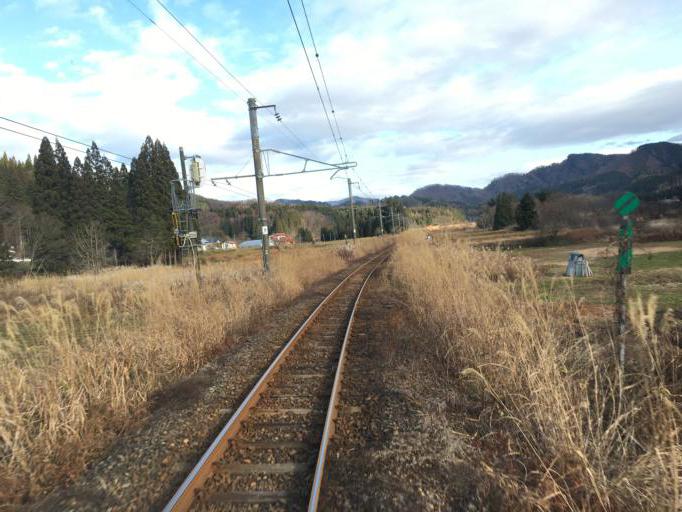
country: JP
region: Yamagata
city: Shinjo
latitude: 38.9736
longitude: 140.3244
